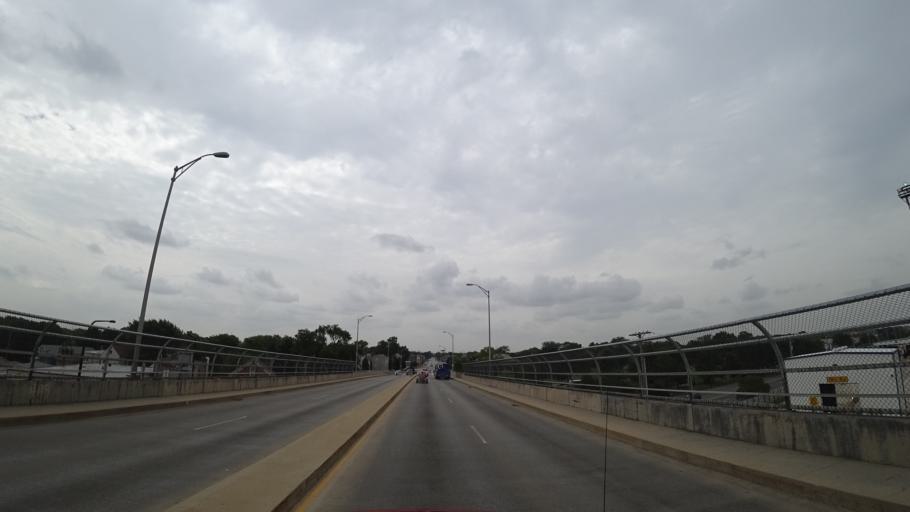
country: US
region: Illinois
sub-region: Cook County
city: Cicero
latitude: 41.8414
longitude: -87.7538
